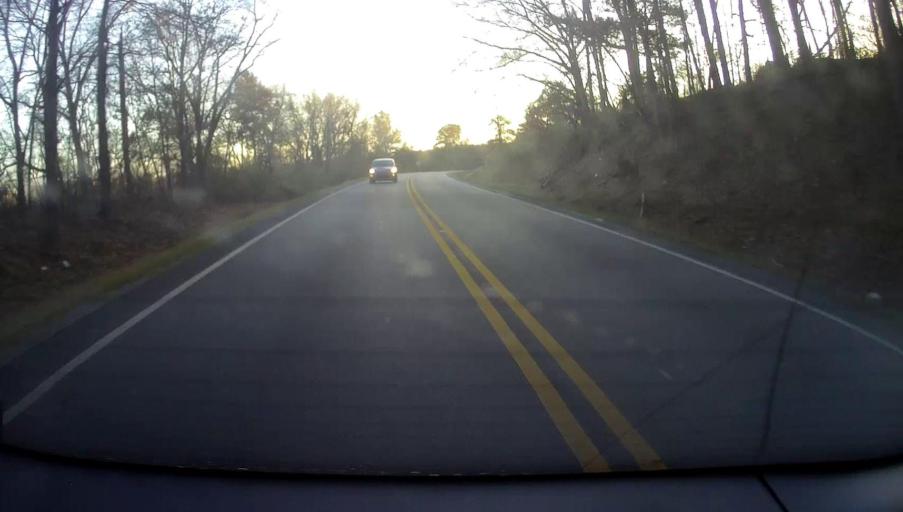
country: US
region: Alabama
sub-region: Etowah County
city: Attalla
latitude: 34.0194
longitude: -86.1174
